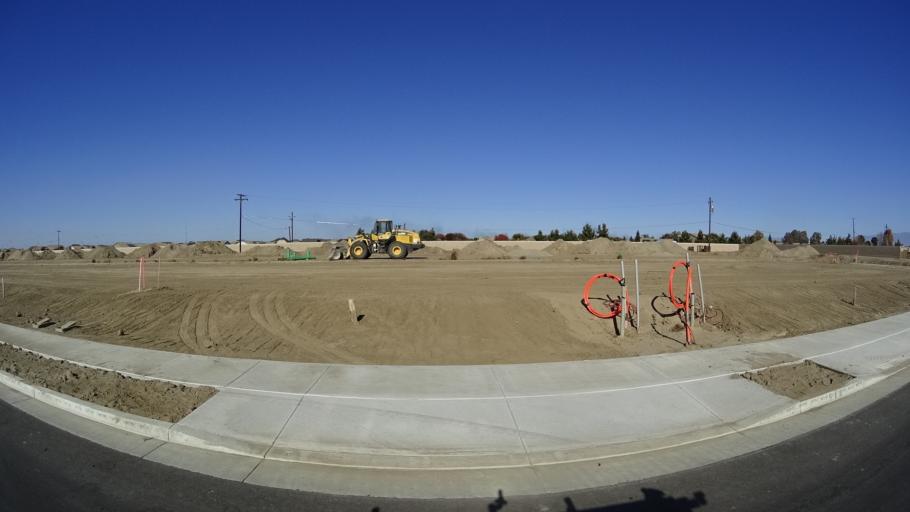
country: US
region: California
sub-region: Kern County
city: Greenfield
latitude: 35.2658
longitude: -119.0674
